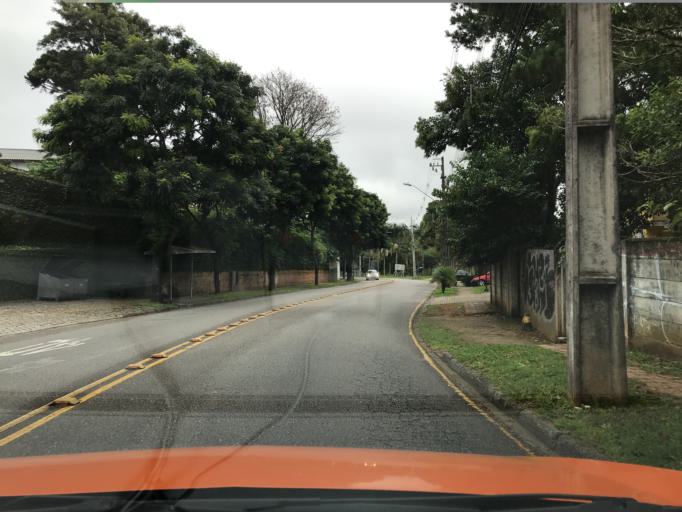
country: BR
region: Parana
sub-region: Curitiba
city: Curitiba
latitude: -25.4237
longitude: -49.3028
